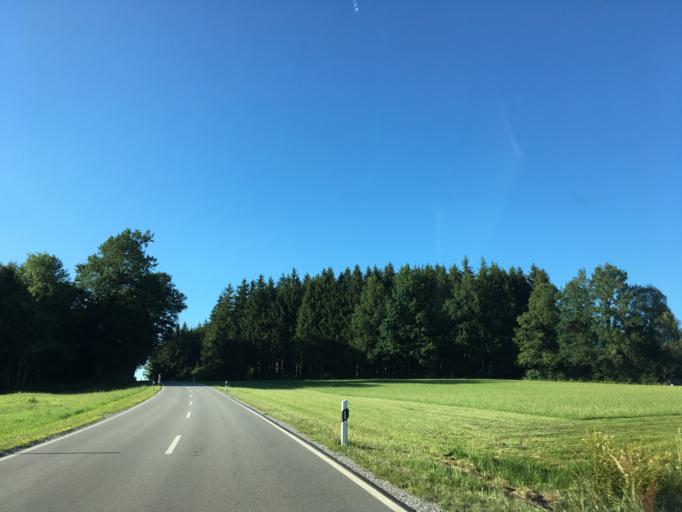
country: DE
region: Bavaria
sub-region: Upper Bavaria
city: Frasdorf
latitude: 47.8232
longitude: 12.2574
